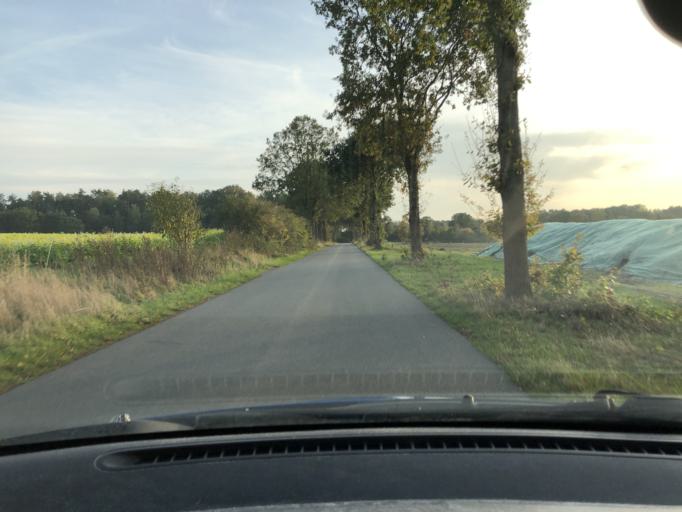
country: DE
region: Lower Saxony
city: Gohrde
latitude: 53.1271
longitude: 10.9453
